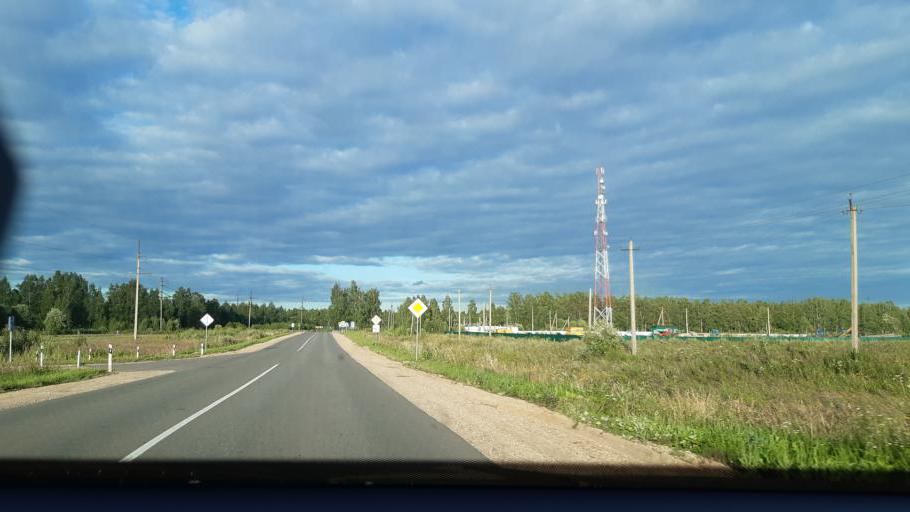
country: RU
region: Smolensk
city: Yel'nya
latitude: 54.5944
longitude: 33.1845
